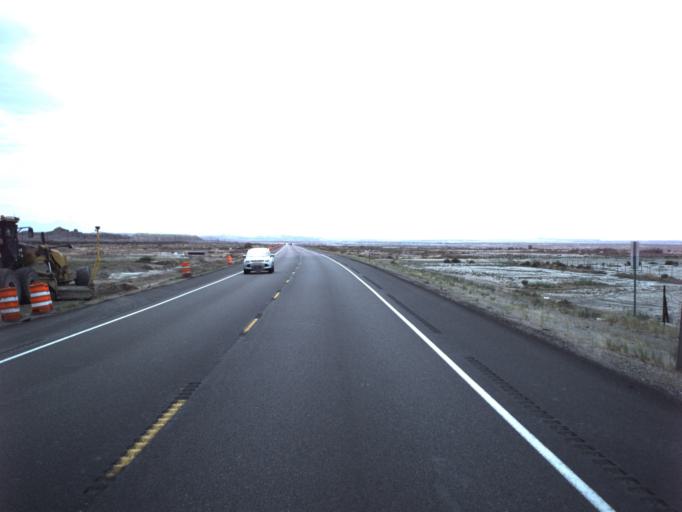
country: US
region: Utah
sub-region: Carbon County
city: East Carbon City
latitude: 39.0247
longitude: -110.2986
